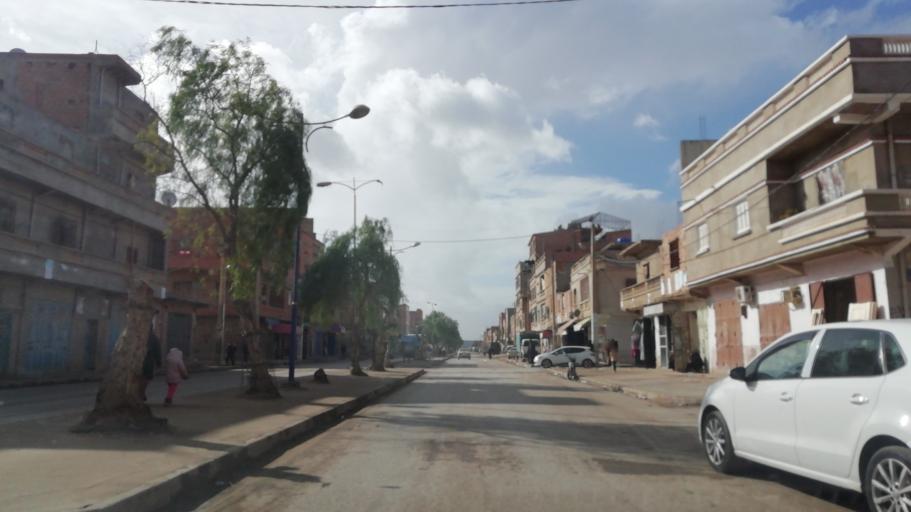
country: DZ
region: Oran
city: Es Senia
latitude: 35.6408
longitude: -0.5743
